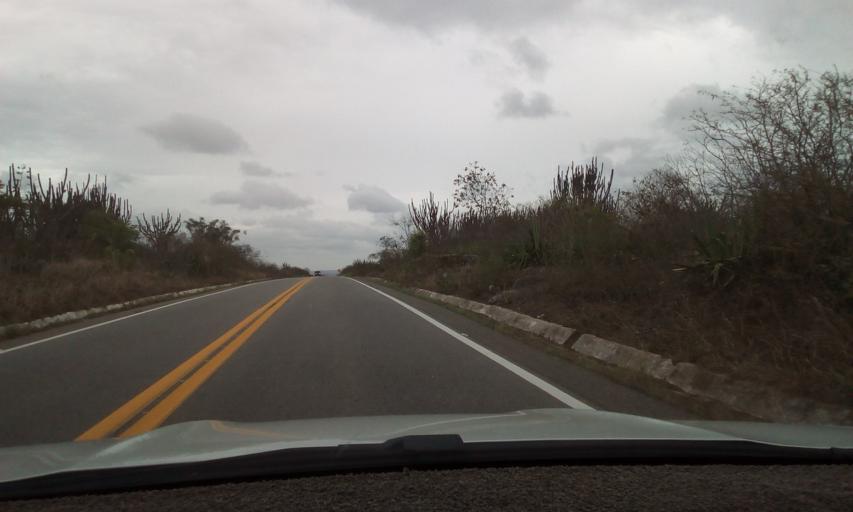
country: BR
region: Paraiba
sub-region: Areia
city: Remigio
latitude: -6.9155
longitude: -35.8547
